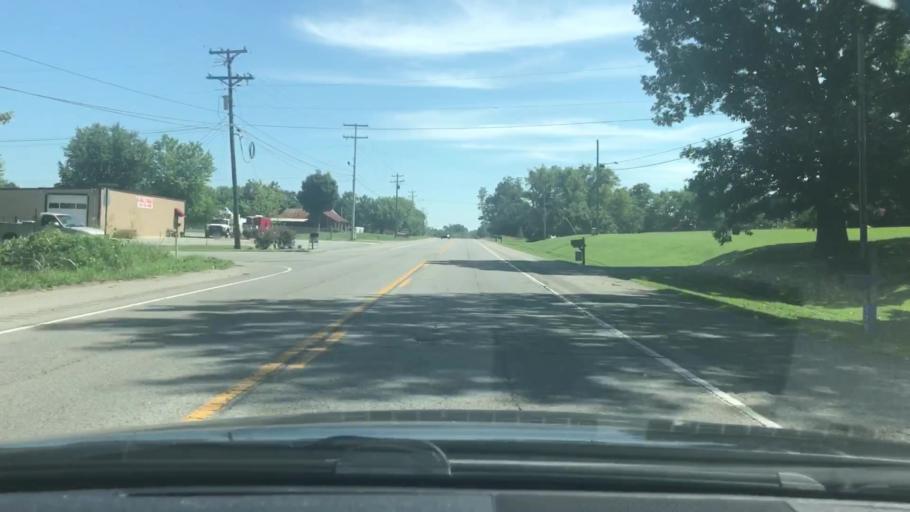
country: US
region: Tennessee
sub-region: Sumner County
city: Millersville
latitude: 36.4167
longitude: -86.6941
